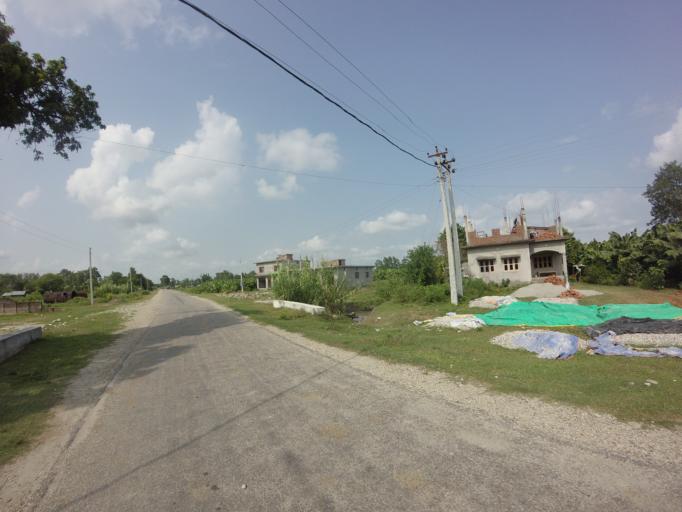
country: NP
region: Far Western
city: Tikapur
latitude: 28.4640
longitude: 81.0757
